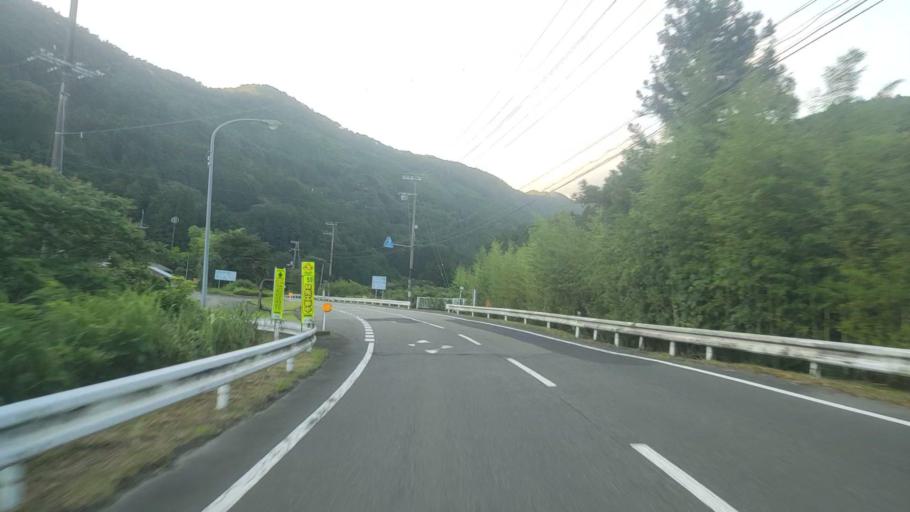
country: JP
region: Wakayama
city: Tanabe
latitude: 33.8228
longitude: 135.6312
